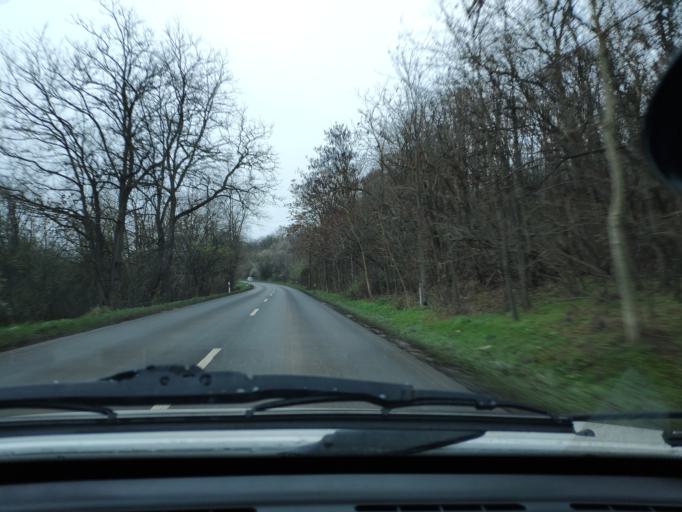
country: HU
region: Pest
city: Biatorbagy
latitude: 47.4534
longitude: 18.8184
